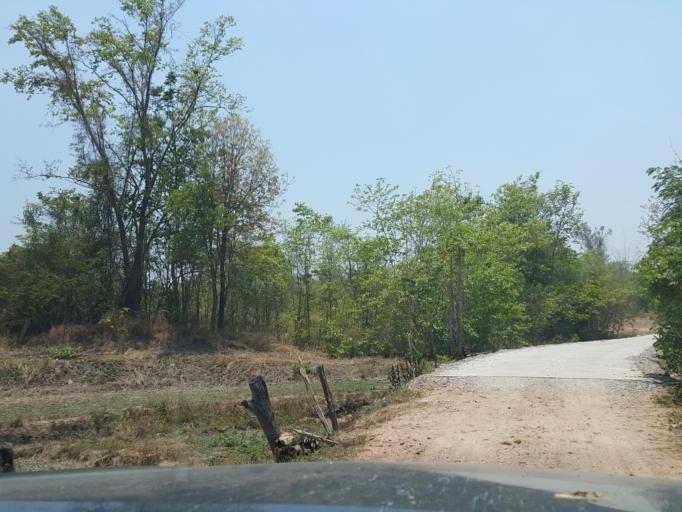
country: TH
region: Lampang
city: Thoen
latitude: 17.6369
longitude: 99.2754
